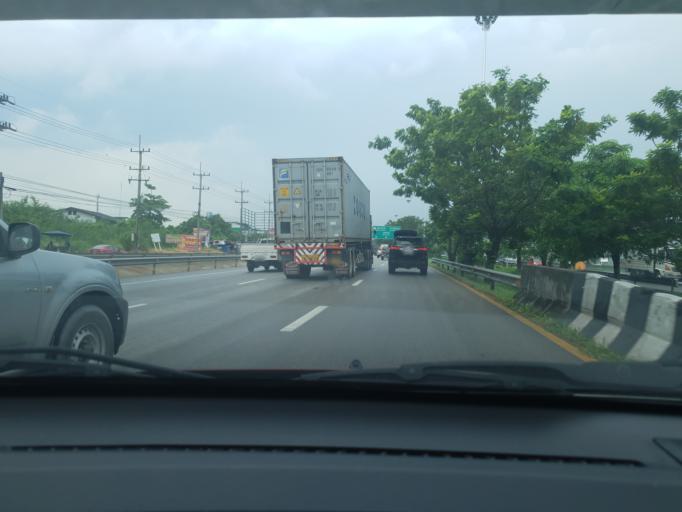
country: TH
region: Samut Sakhon
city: Samut Sakhon
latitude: 13.5855
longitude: 100.3185
